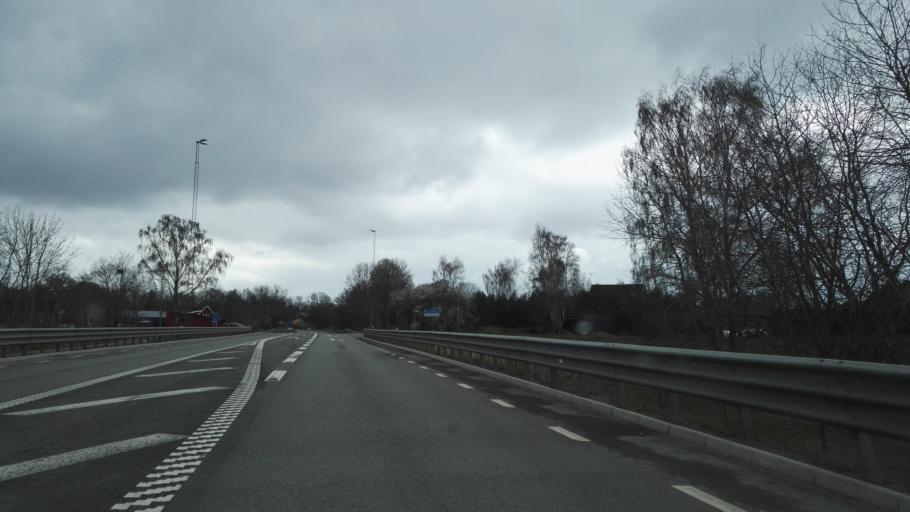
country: SE
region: Skane
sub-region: Hassleholms Kommun
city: Hassleholm
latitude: 56.1498
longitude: 13.8073
